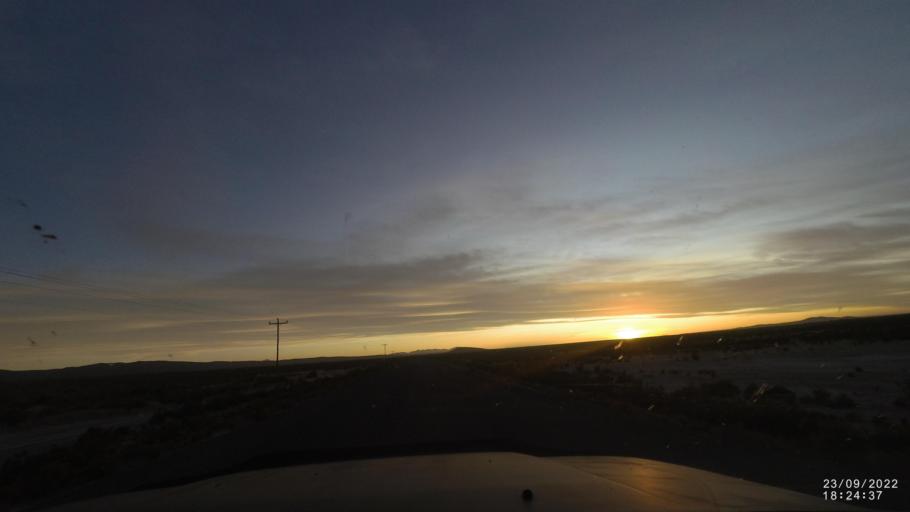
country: BO
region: Oruro
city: Challapata
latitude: -19.3044
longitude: -67.1239
